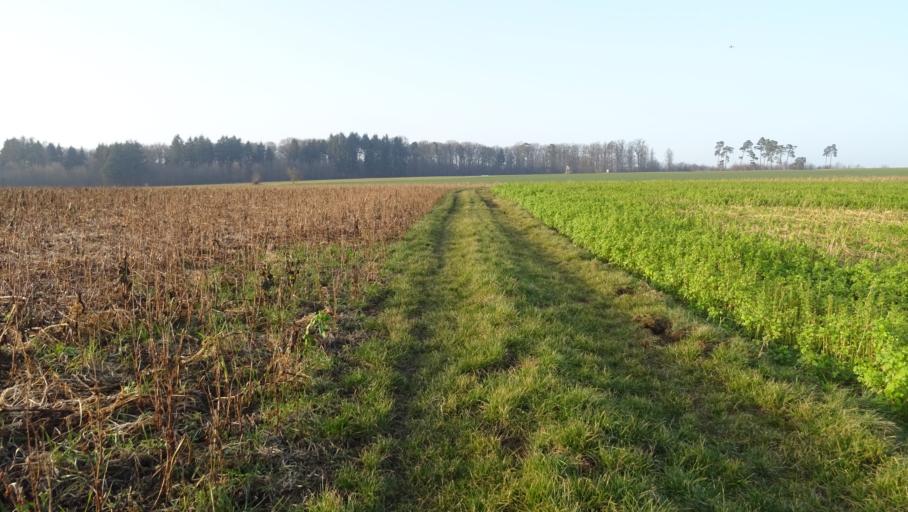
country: DE
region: Baden-Wuerttemberg
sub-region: Karlsruhe Region
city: Fahrenbach
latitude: 49.4019
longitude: 9.1141
